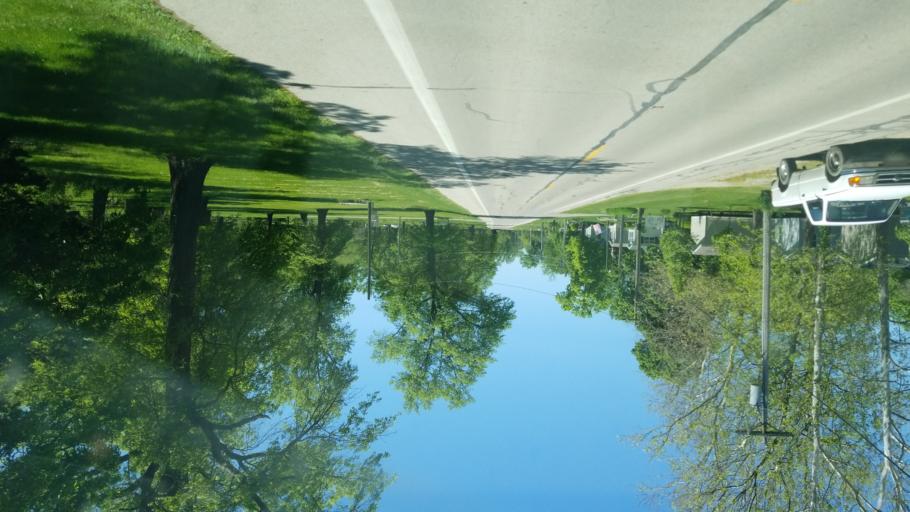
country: US
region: Ohio
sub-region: Shelby County
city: Fort Loramie
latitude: 40.3727
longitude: -84.3626
